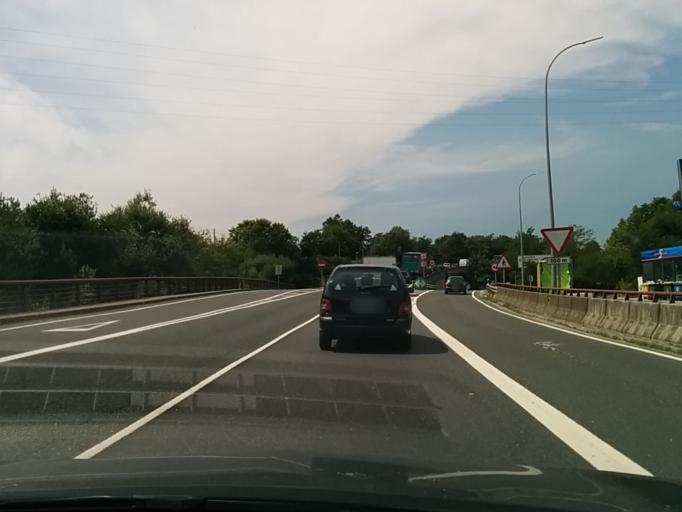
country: ES
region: Basque Country
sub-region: Provincia de Guipuzcoa
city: Lezo
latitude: 43.3119
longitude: -1.8795
